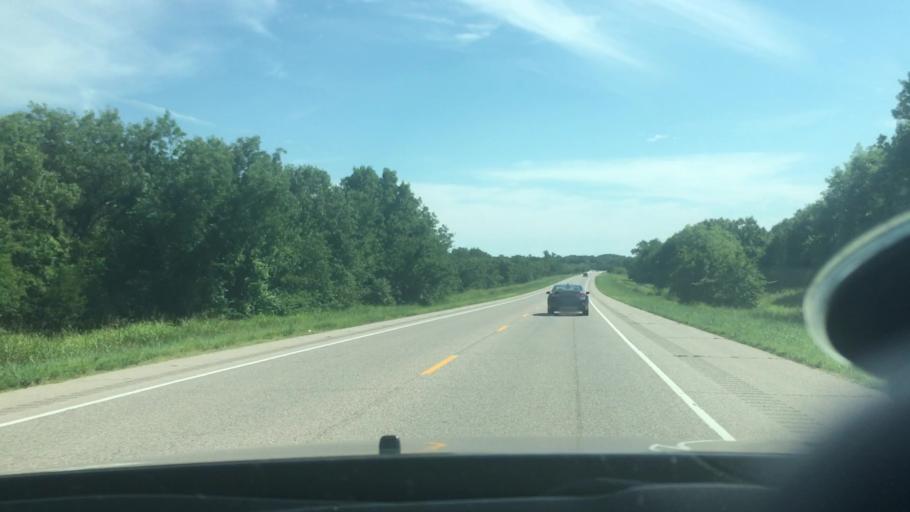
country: US
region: Oklahoma
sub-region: Seminole County
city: Maud
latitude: 35.0629
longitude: -96.6793
